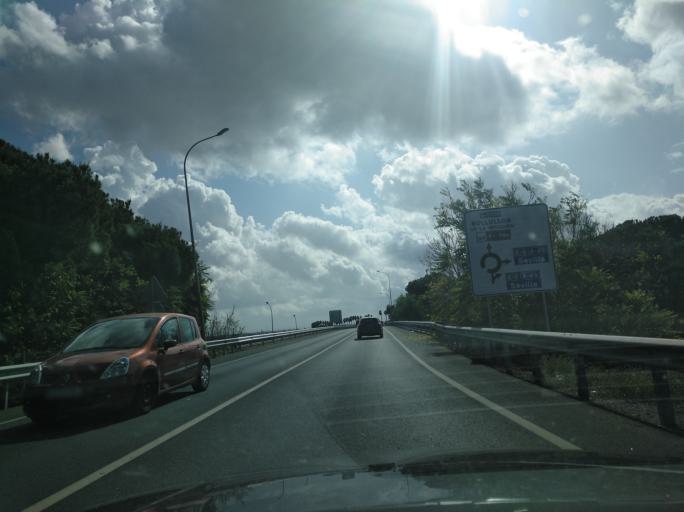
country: ES
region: Andalusia
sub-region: Provincia de Sevilla
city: Umbrete
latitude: 37.3605
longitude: -6.1420
